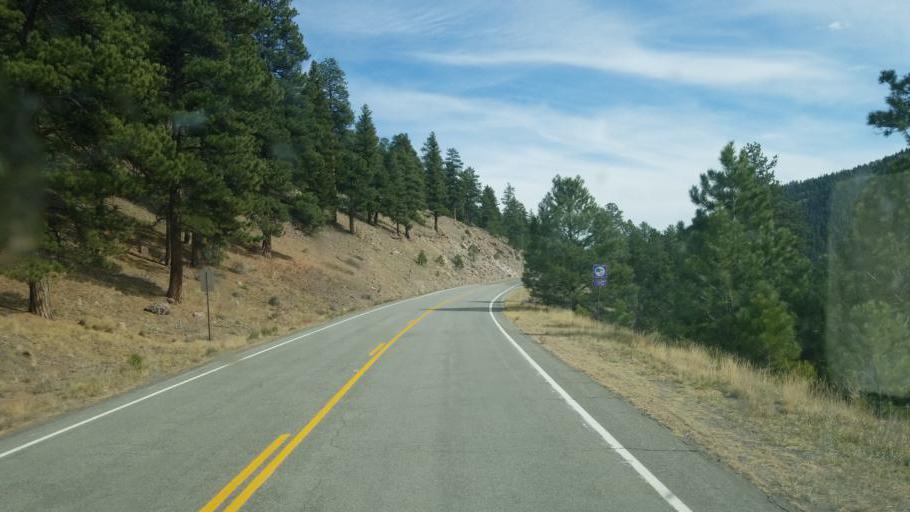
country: US
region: Colorado
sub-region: Conejos County
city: Conejos
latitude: 37.0761
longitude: -106.2855
